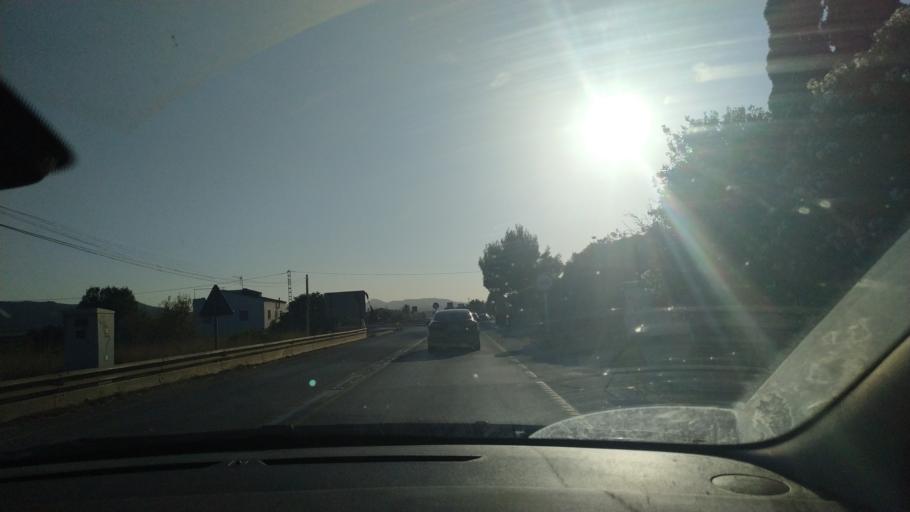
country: ES
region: Valencia
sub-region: Provincia de Alicante
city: Javea
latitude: 38.7754
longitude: 0.1423
